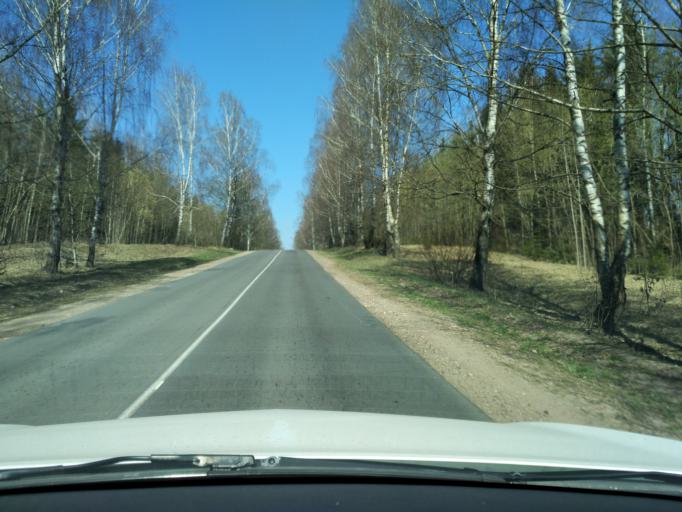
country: BY
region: Minsk
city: Slabada
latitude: 53.9743
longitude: 27.9521
